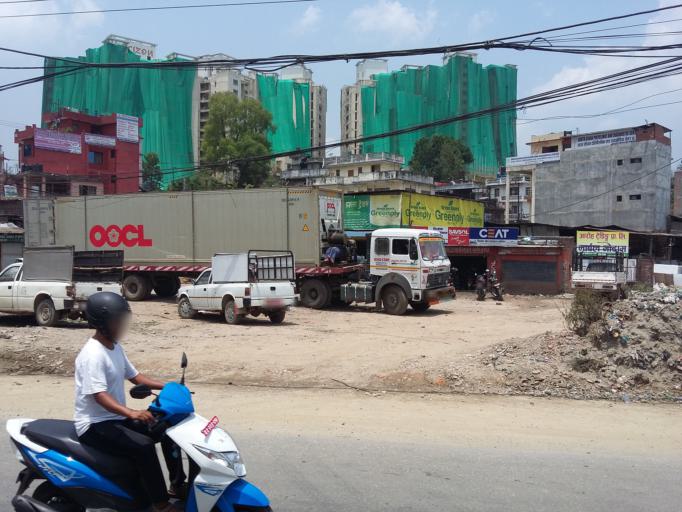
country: NP
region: Central Region
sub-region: Bagmati Zone
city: Kathmandu
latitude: 27.7387
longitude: 85.3261
